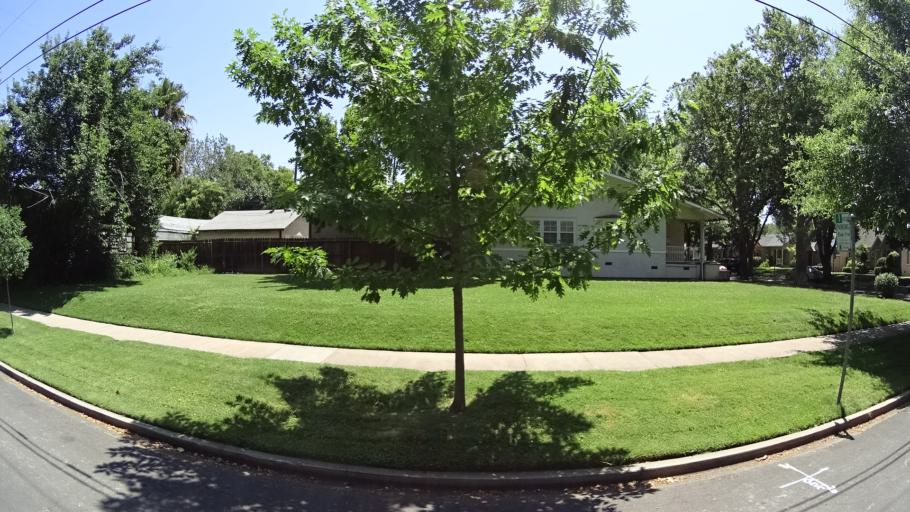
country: US
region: California
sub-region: Sacramento County
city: Sacramento
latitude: 38.5528
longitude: -121.4913
